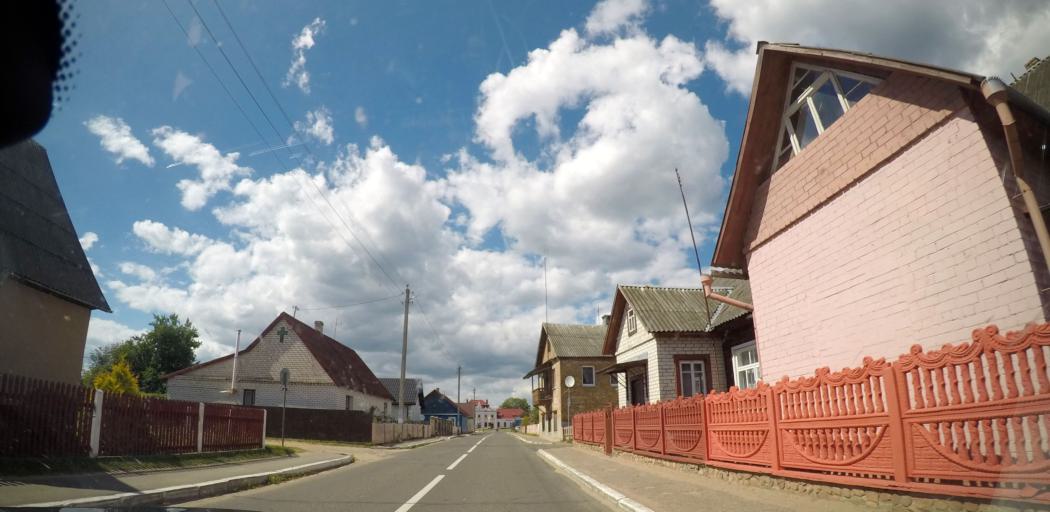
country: LT
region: Alytaus apskritis
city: Druskininkai
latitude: 53.8843
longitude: 24.1372
